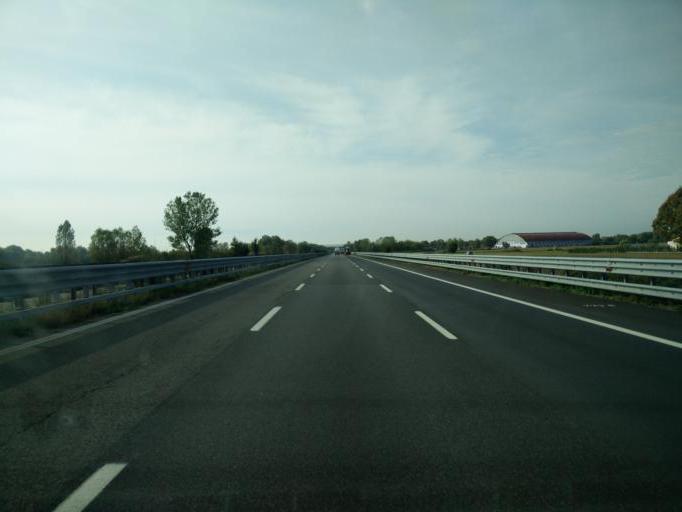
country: IT
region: Lombardy
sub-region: Provincia di Brescia
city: Leno
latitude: 45.3820
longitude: 10.1781
